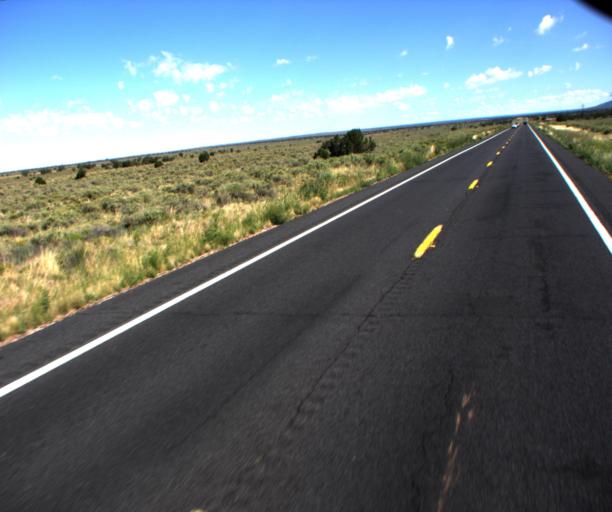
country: US
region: Arizona
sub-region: Coconino County
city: Grand Canyon Village
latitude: 35.6885
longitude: -112.1345
